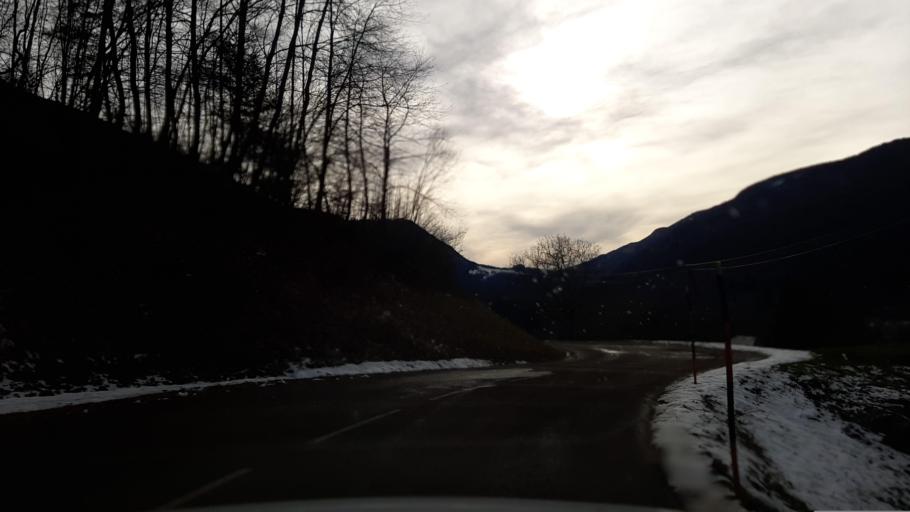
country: FR
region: Rhone-Alpes
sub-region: Departement de la Savoie
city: Cruet
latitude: 45.6440
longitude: 6.0917
